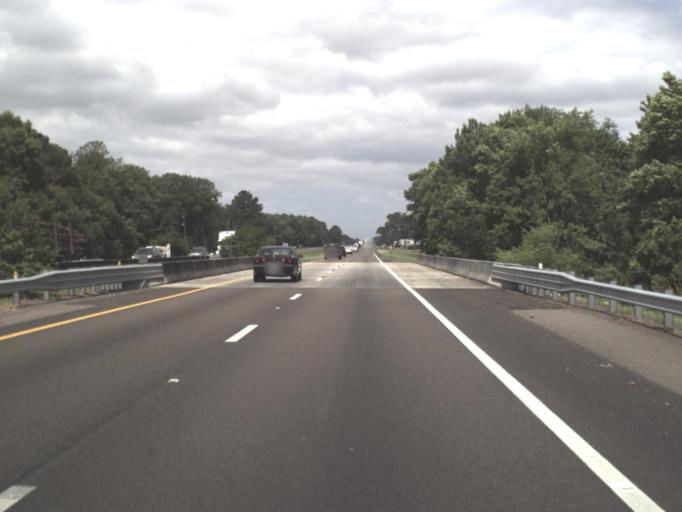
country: US
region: Florida
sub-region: Nassau County
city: Yulee
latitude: 30.6297
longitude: -81.5702
